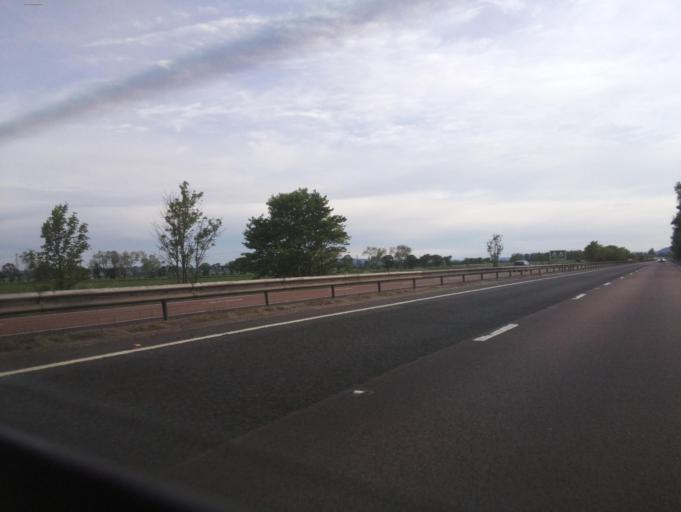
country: GB
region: Scotland
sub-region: Perth and Kinross
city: Errol
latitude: 56.4362
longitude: -3.1921
